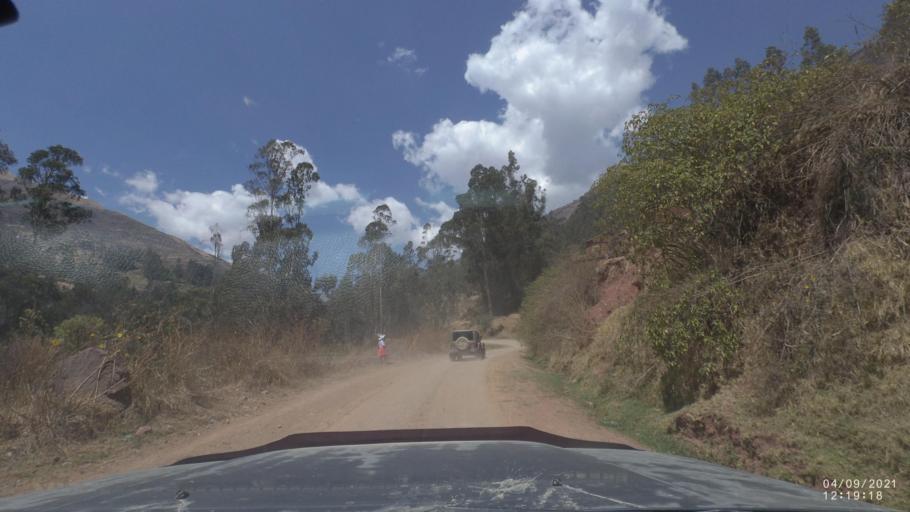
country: BO
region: Cochabamba
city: Colchani
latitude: -17.2370
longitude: -66.5300
